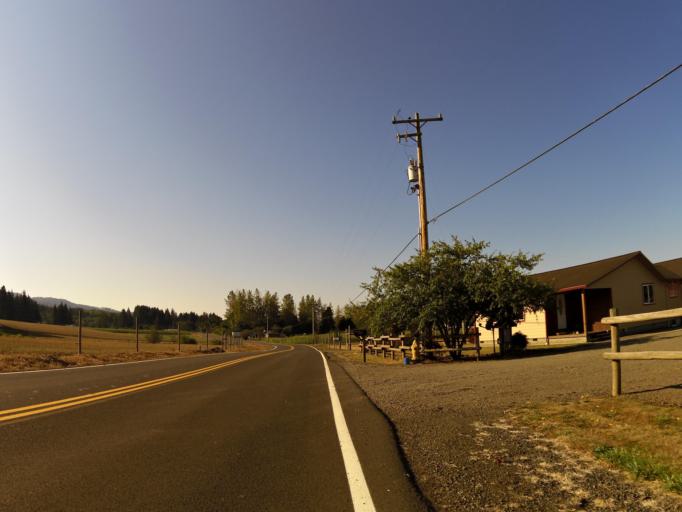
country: US
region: Oregon
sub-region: Tillamook County
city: Tillamook
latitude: 45.3927
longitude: -123.7936
